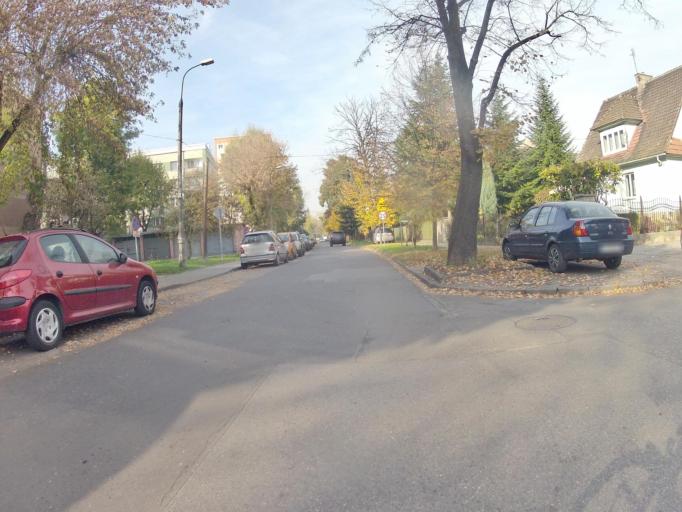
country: PL
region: Lesser Poland Voivodeship
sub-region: Krakow
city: Krakow
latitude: 50.0593
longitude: 19.9808
